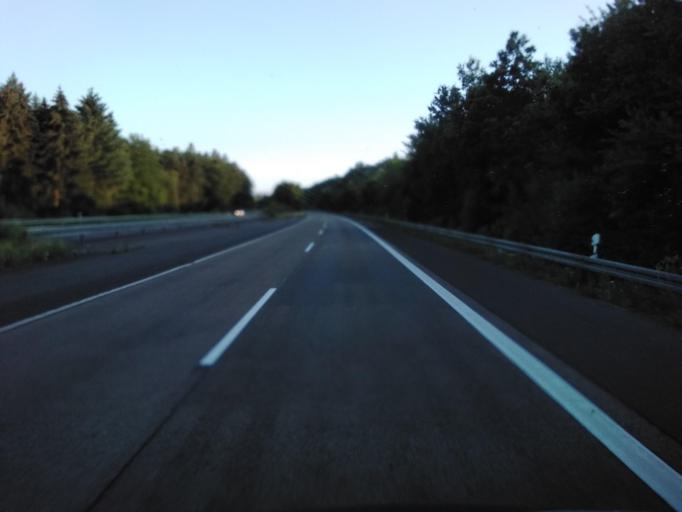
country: DE
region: Hesse
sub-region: Regierungsbezirk Darmstadt
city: Echzell
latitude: 50.3948
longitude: 8.9328
